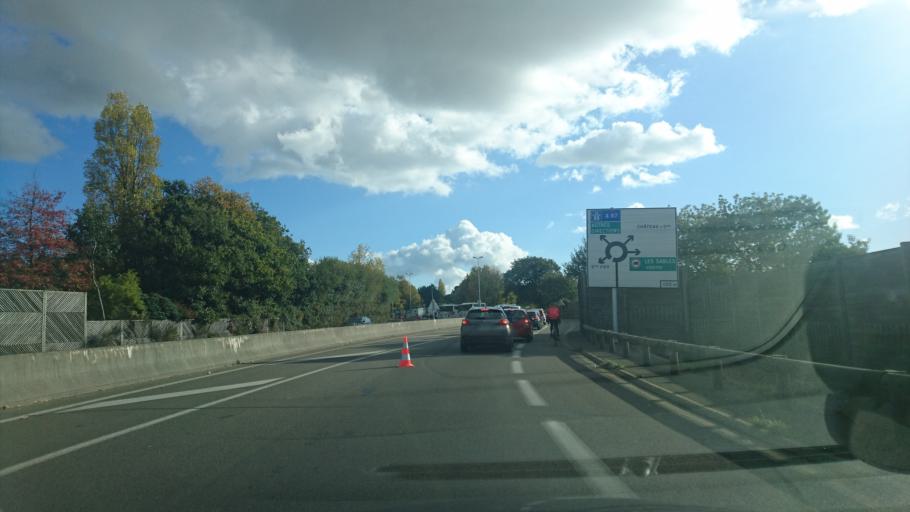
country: FR
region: Pays de la Loire
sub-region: Departement de la Vendee
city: Olonne-sur-Mer
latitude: 46.5164
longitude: -1.7601
